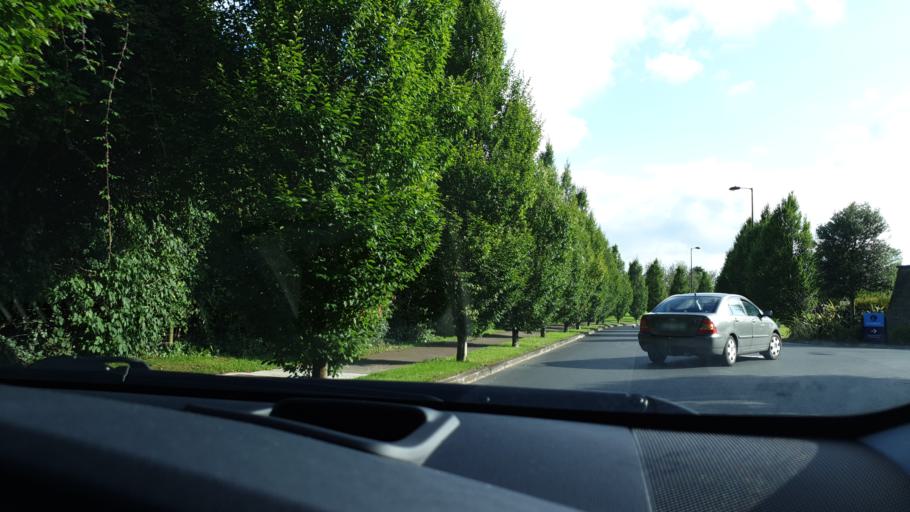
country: IE
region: Leinster
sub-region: An Mhi
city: Ashbourne
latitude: 53.5084
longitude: -6.4041
